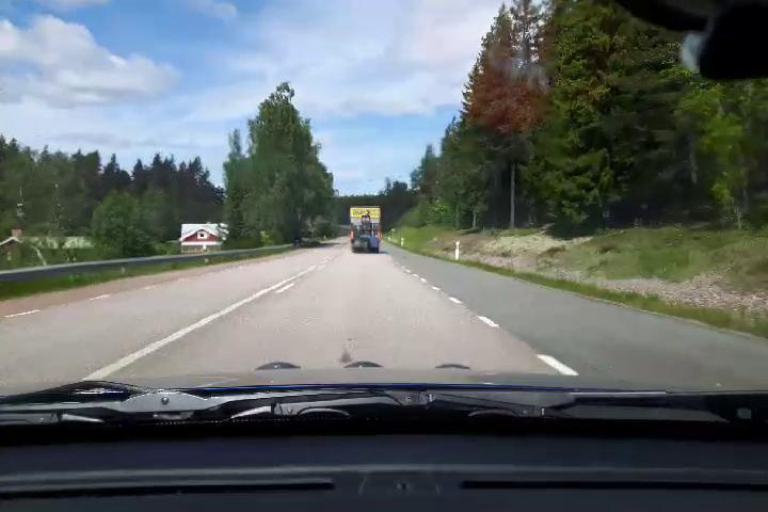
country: SE
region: Uppsala
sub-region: Osthammars Kommun
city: Bjorklinge
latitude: 60.0954
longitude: 17.5540
